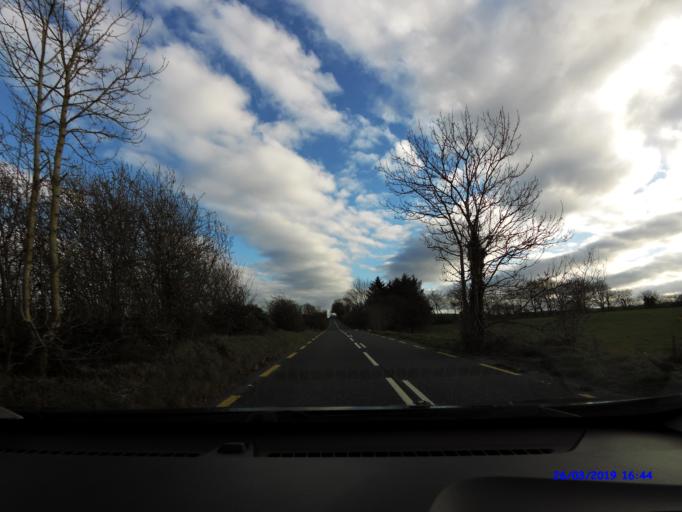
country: IE
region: Connaught
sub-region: Maigh Eo
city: Ballyhaunis
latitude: 53.8464
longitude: -8.7656
